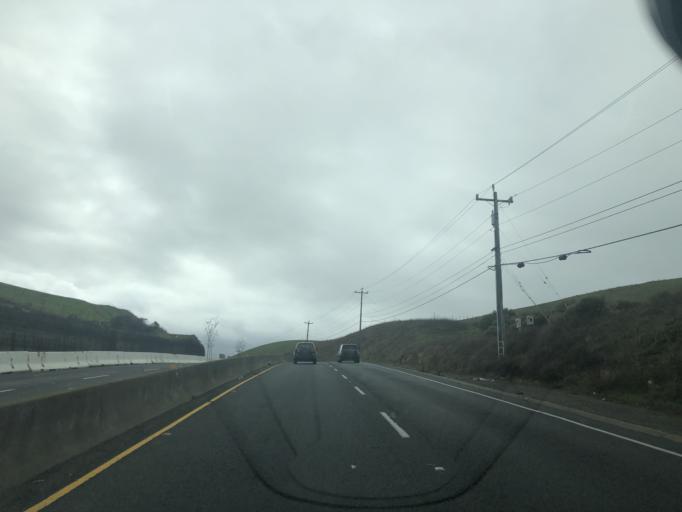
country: US
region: California
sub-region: Contra Costa County
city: Clayton
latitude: 37.9681
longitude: -121.9259
